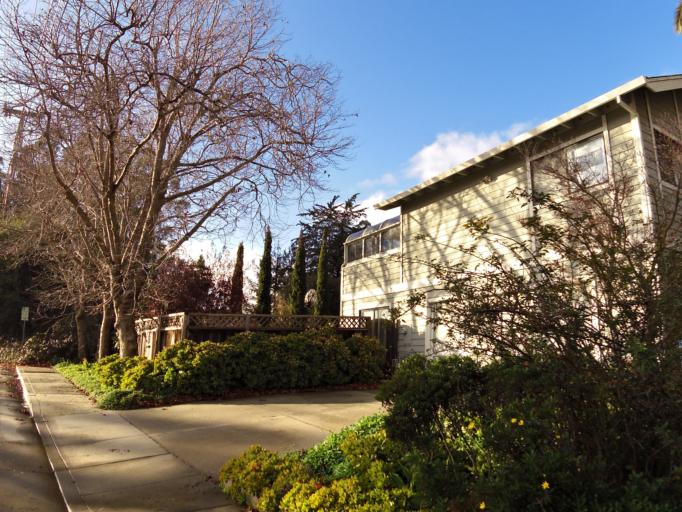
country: US
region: California
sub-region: Santa Cruz County
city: Santa Cruz
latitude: 36.9747
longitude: -122.0587
